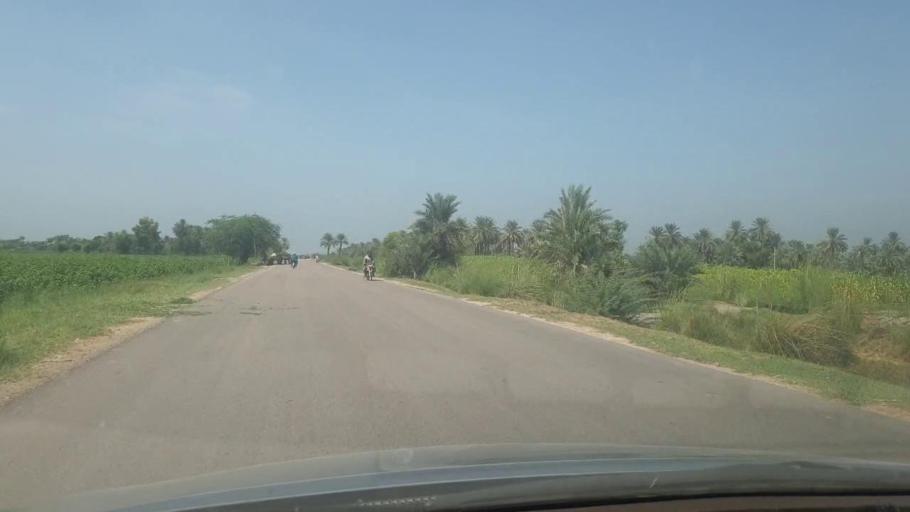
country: PK
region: Sindh
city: Ranipur
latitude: 27.2447
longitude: 68.5774
